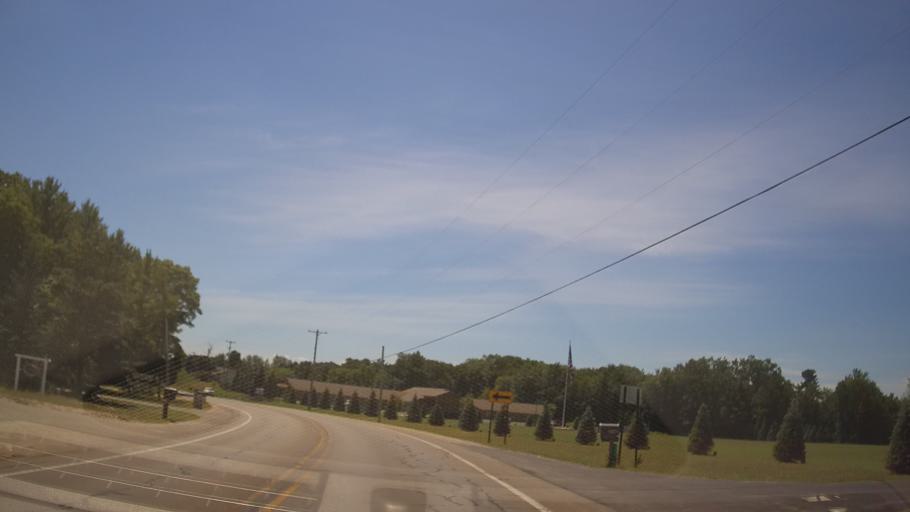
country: US
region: Michigan
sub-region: Grand Traverse County
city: Traverse City
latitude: 44.7131
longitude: -85.6891
